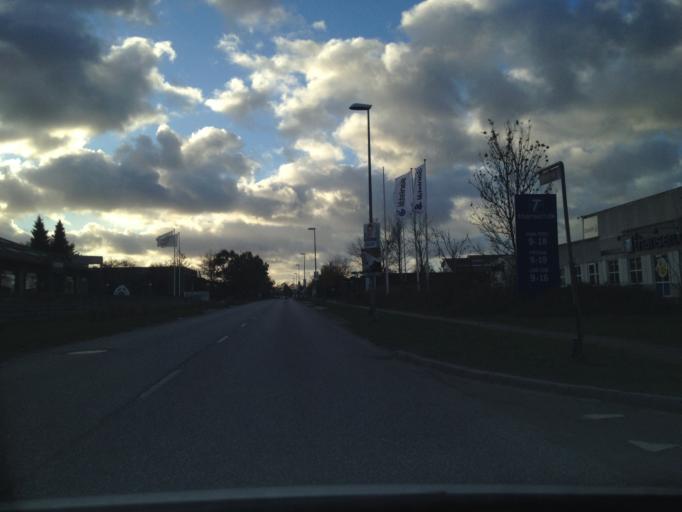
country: DK
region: Capital Region
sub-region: Hillerod Kommune
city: Hillerod
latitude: 55.9322
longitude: 12.2689
